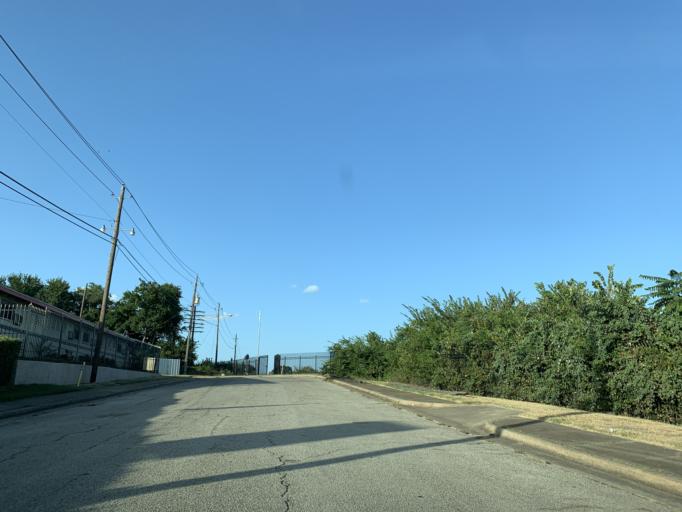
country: US
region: Texas
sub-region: Dallas County
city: Dallas
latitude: 32.7587
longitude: -96.7413
